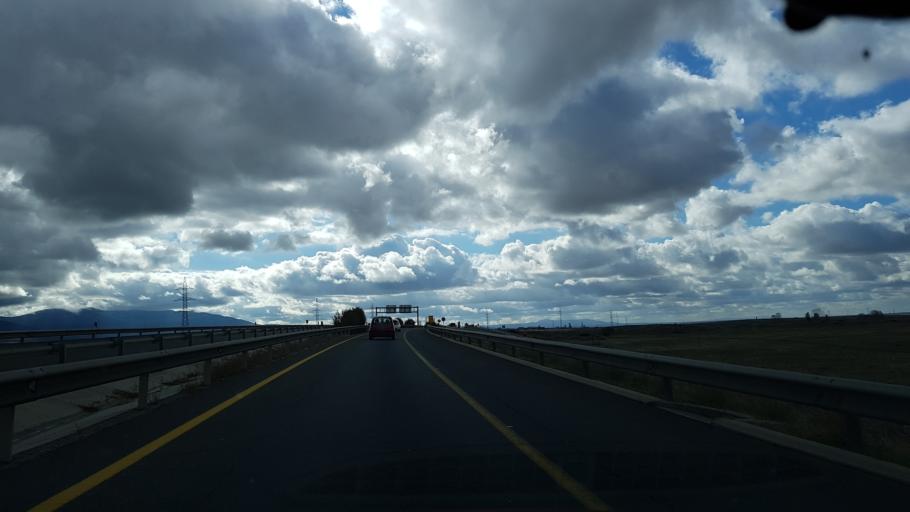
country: ES
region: Castille and Leon
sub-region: Provincia de Segovia
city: Palazuelos de Eresma
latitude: 40.9260
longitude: -4.0881
